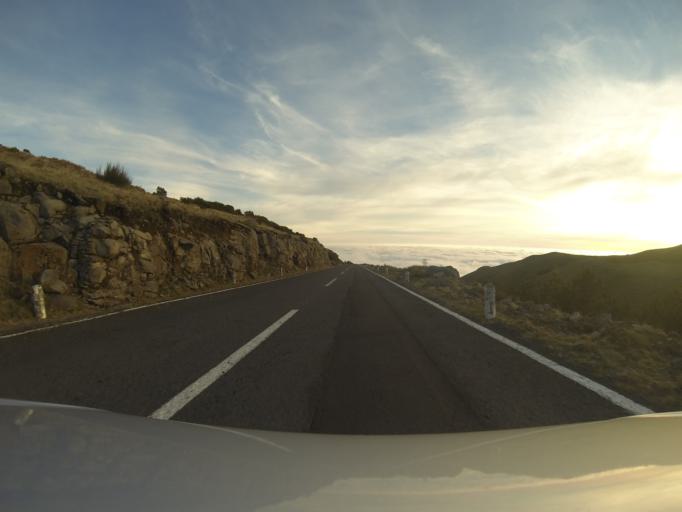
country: PT
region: Madeira
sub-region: Sao Vicente
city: Sao Vicente
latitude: 32.7356
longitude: -17.0614
